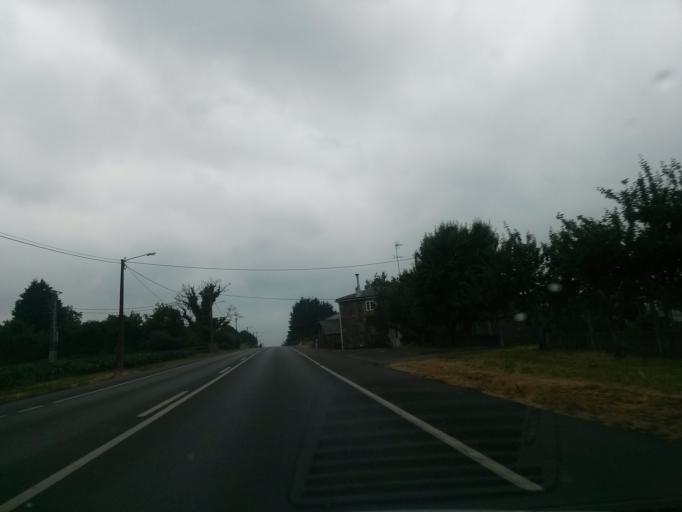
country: ES
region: Galicia
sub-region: Provincia de Lugo
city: Begonte
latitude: 43.1341
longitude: -7.6562
